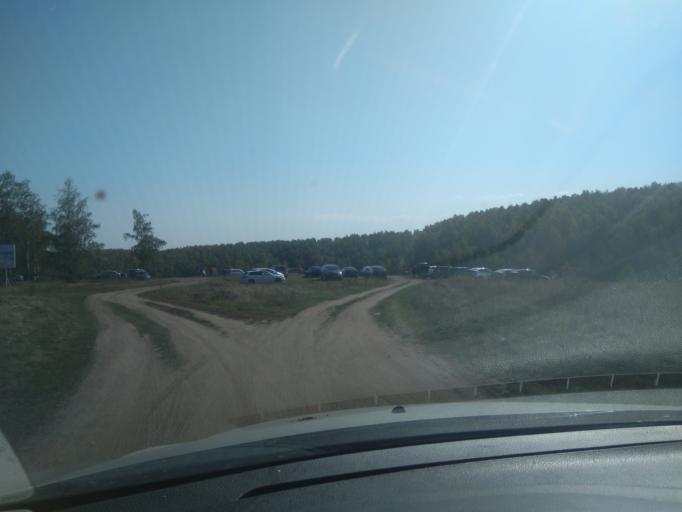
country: RU
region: Sverdlovsk
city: Pokrovskoye
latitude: 56.4349
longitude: 61.6028
